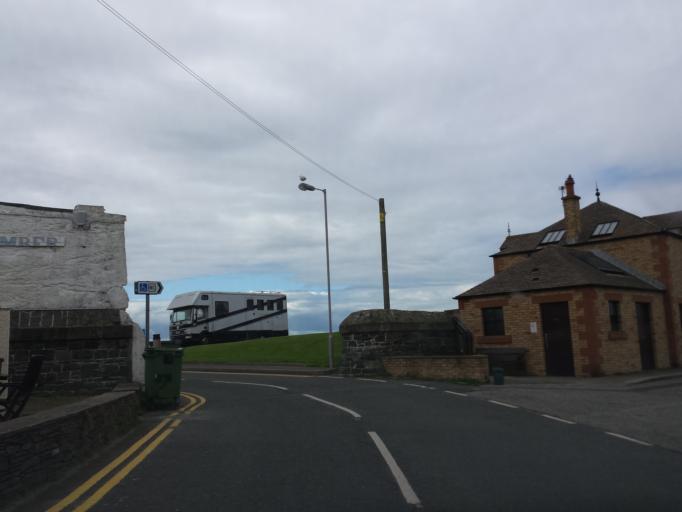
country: GB
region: Scotland
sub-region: Dumfries and Galloway
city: Stranraer
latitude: 54.8405
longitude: -5.1167
